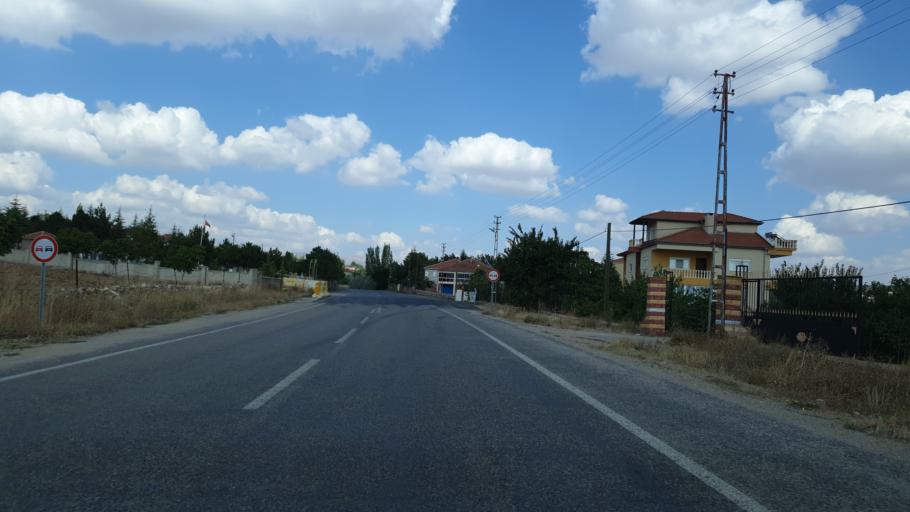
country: TR
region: Kayseri
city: Felahiye
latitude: 39.1059
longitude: 35.5976
